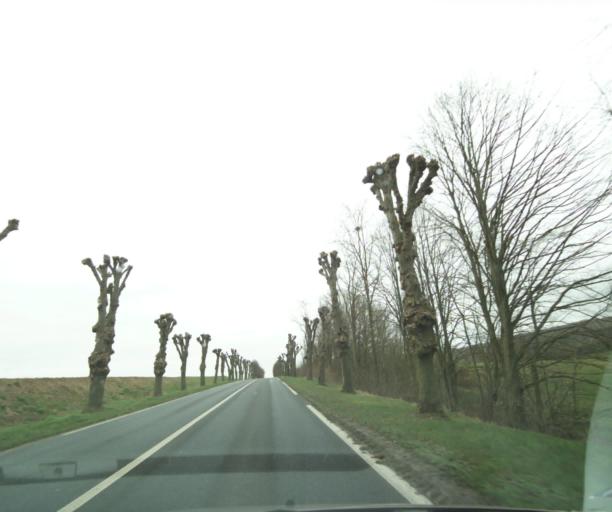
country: FR
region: Picardie
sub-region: Departement de l'Oise
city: Crisolles
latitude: 49.6044
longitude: 3.0143
